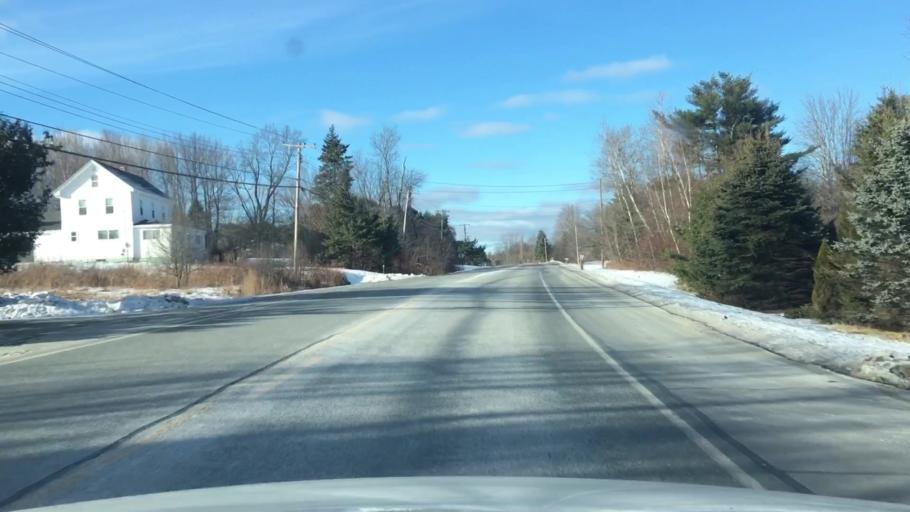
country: US
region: Maine
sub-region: Penobscot County
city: Eddington
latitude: 44.8193
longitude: -68.6476
